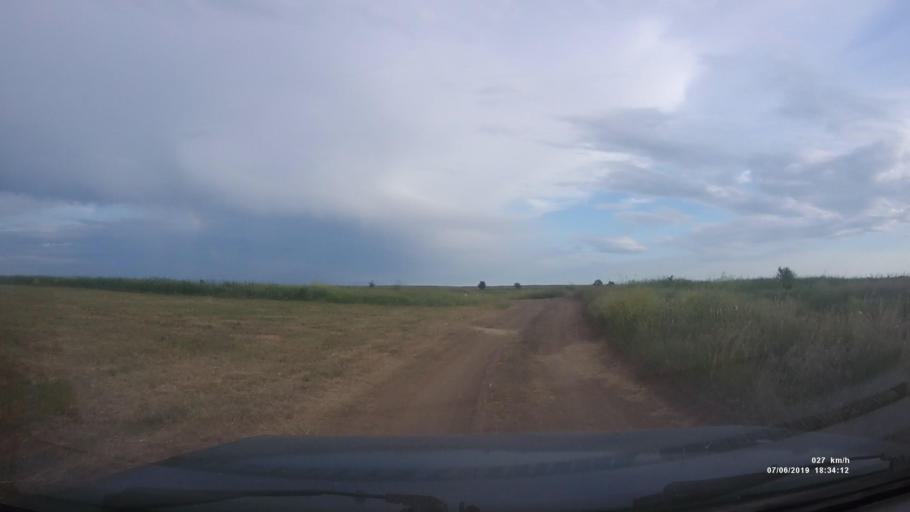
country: RU
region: Rostov
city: Staraya Stanitsa
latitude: 48.2588
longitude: 40.3622
